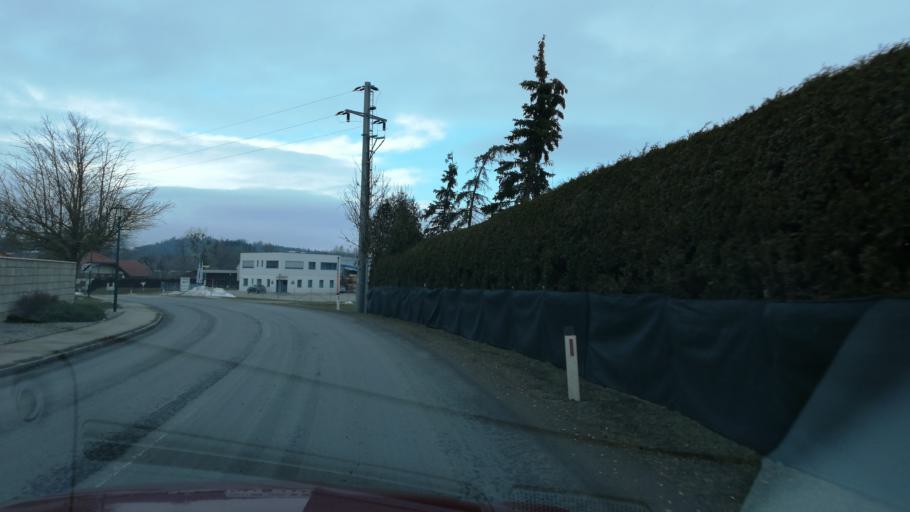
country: AT
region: Upper Austria
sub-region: Politischer Bezirk Vocklabruck
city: Wolfsegg am Hausruck
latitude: 48.1771
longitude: 13.6949
